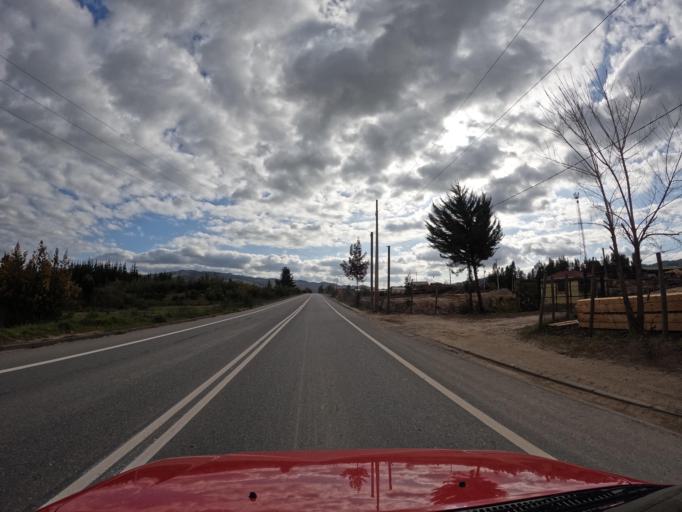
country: CL
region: Maule
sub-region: Provincia de Talca
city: Constitucion
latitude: -35.5564
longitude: -72.1138
